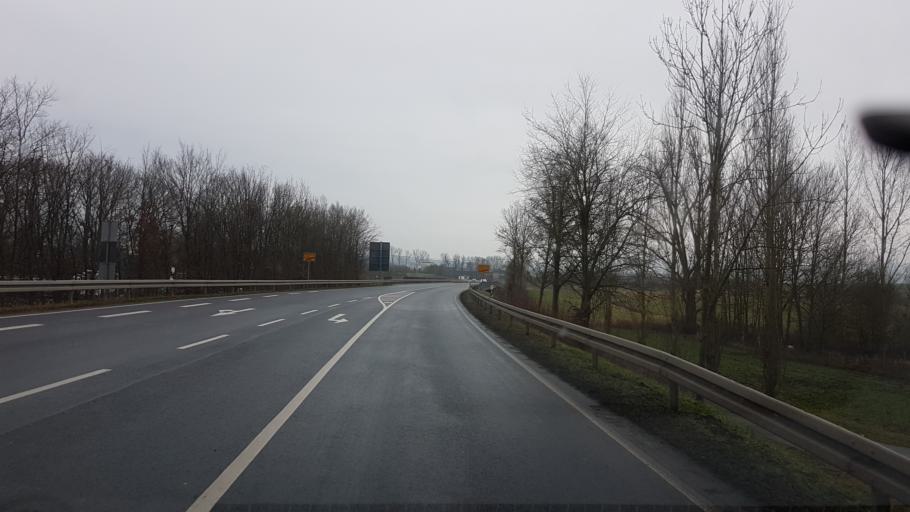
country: DE
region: Bavaria
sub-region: Regierungsbezirk Unterfranken
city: Bad Konigshofen im Grabfeld
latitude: 50.2974
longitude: 10.4632
